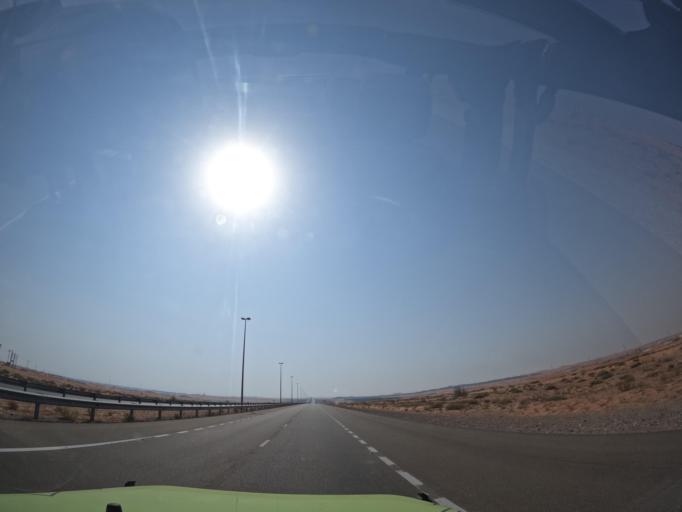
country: OM
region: Al Buraimi
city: Al Buraymi
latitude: 24.4134
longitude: 55.6984
